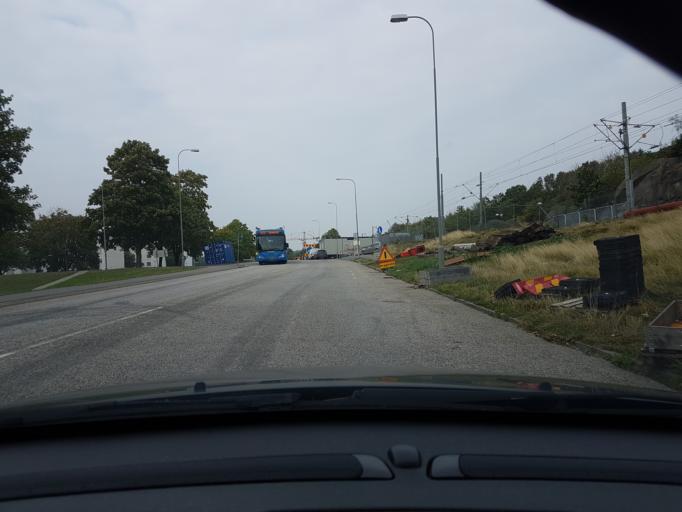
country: SE
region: Vaestra Goetaland
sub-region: Goteborg
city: Majorna
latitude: 57.6480
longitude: 11.9029
